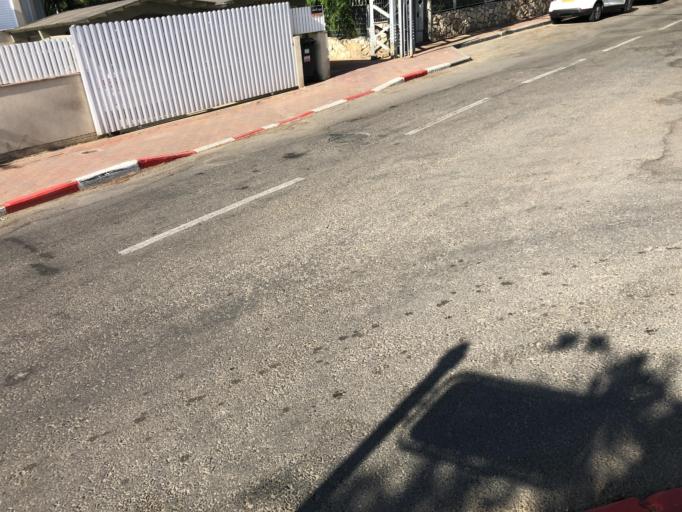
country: IL
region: Central District
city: Yehud
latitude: 32.0356
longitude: 34.8957
